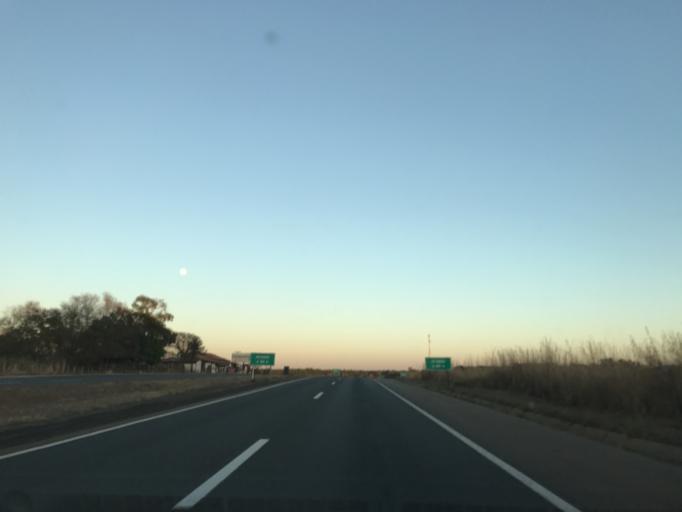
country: BR
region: Goias
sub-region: Abadiania
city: Abadiania
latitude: -16.1891
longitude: -48.6820
